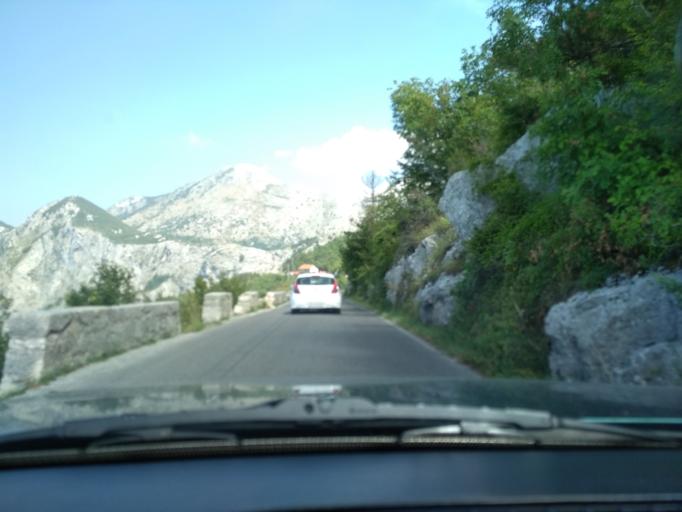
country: ME
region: Kotor
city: Kotor
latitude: 42.4160
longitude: 18.7922
